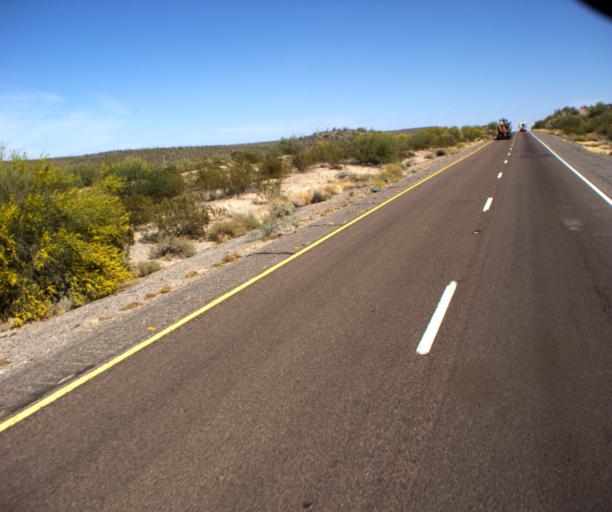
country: US
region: Arizona
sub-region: Pinal County
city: Maricopa
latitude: 32.8497
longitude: -112.3410
